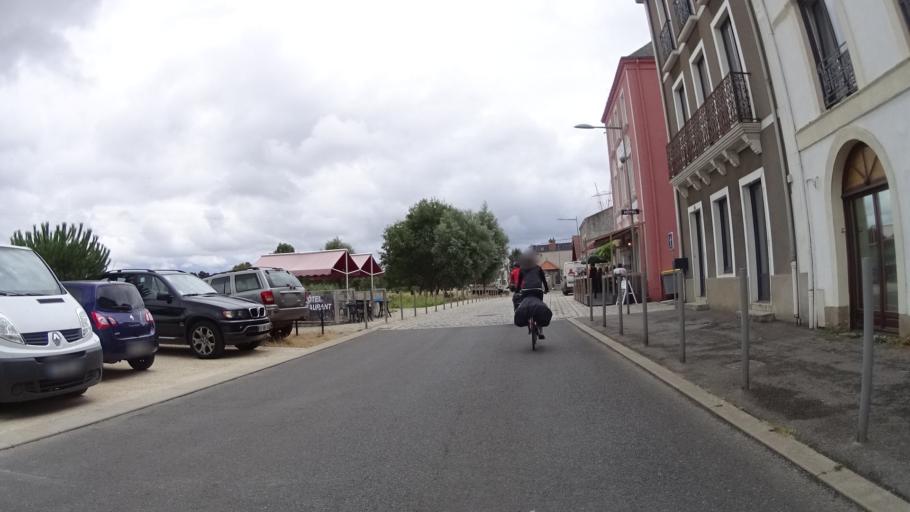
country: FR
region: Pays de la Loire
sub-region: Departement de la Loire-Atlantique
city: Le Pellerin
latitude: 47.2022
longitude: -1.7524
